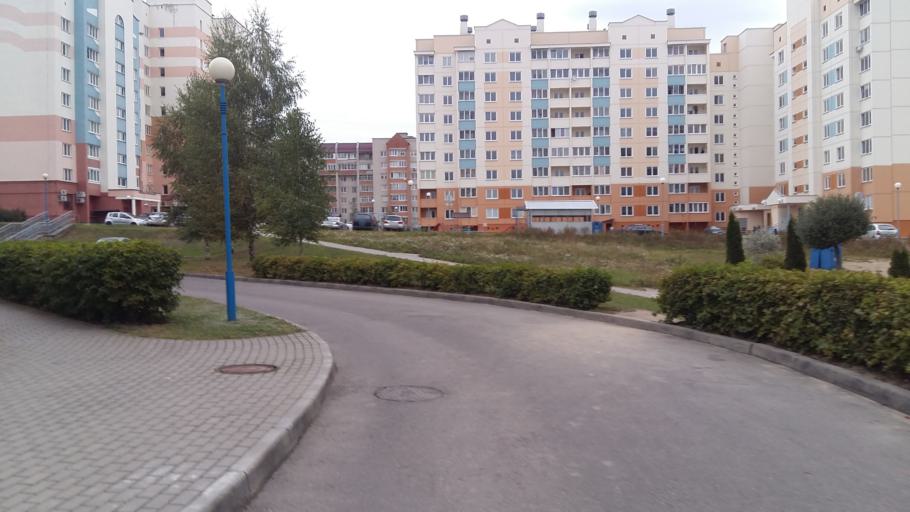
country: BY
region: Grodnenskaya
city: Hrodna
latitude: 53.7099
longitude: 23.8512
